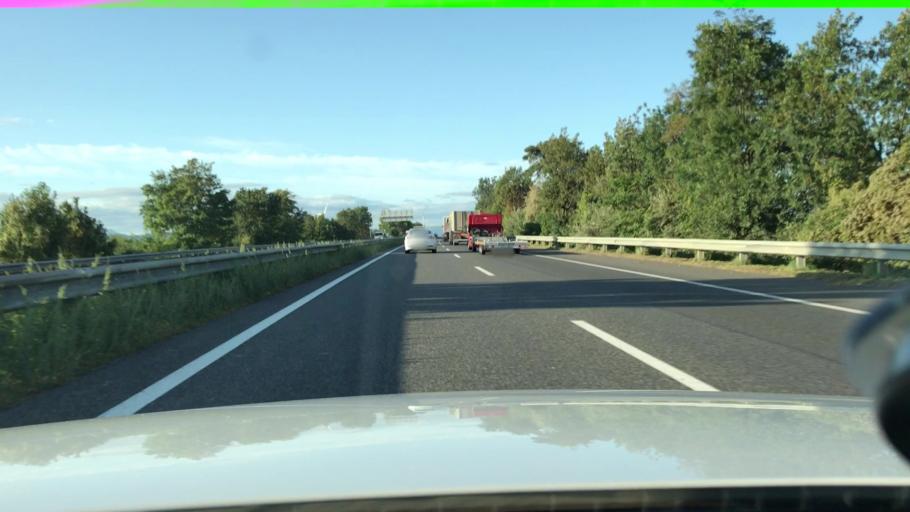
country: AT
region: Lower Austria
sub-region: Sankt Polten Stadt
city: Sankt Poelten
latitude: 48.2209
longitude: 15.6770
